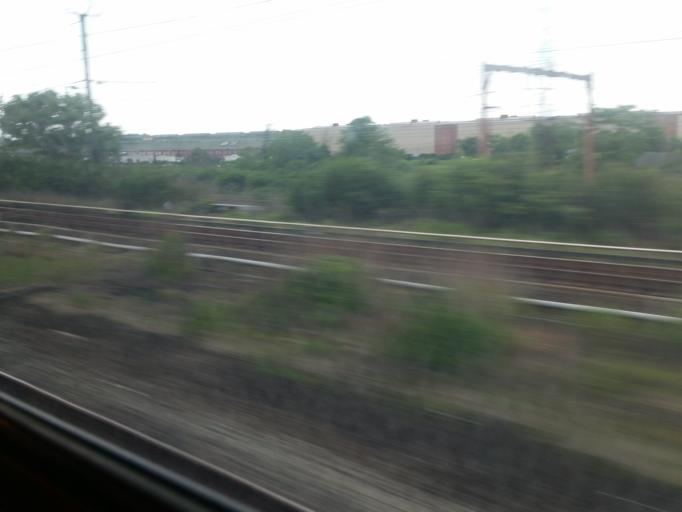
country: US
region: New Jersey
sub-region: Hudson County
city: Harrison
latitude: 40.7424
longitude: -74.1407
